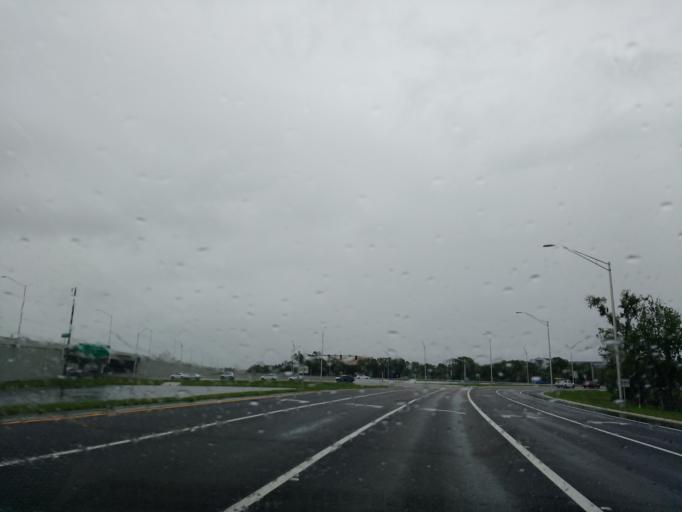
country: US
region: Florida
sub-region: Sarasota County
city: The Meadows
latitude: 27.3871
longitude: -82.4474
